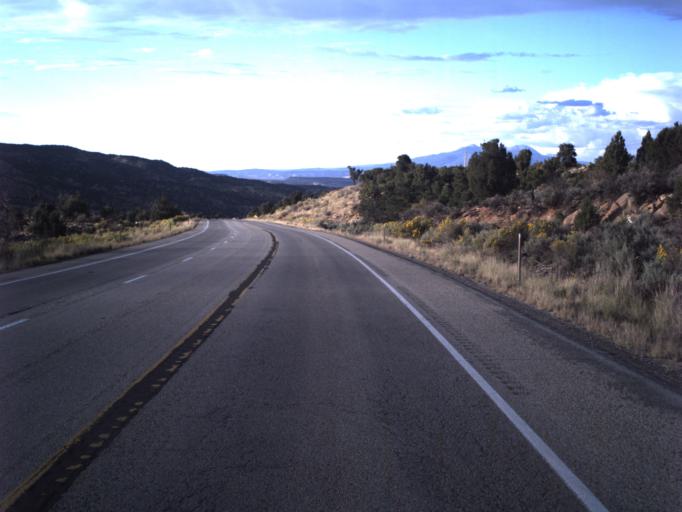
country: US
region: Utah
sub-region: San Juan County
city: Monticello
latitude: 37.9919
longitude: -109.3530
